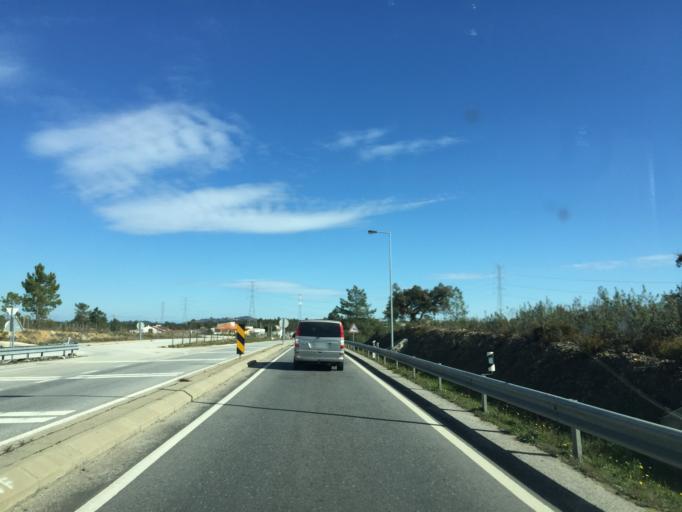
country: PT
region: Castelo Branco
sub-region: Castelo Branco
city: Castelo Branco
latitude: 39.7861
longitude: -7.5679
